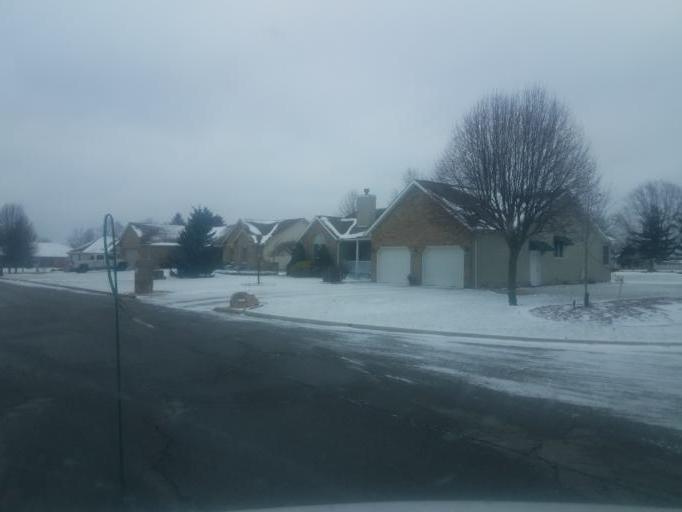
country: US
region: Ohio
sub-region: Richland County
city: Ontario
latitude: 40.7548
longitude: -82.6494
